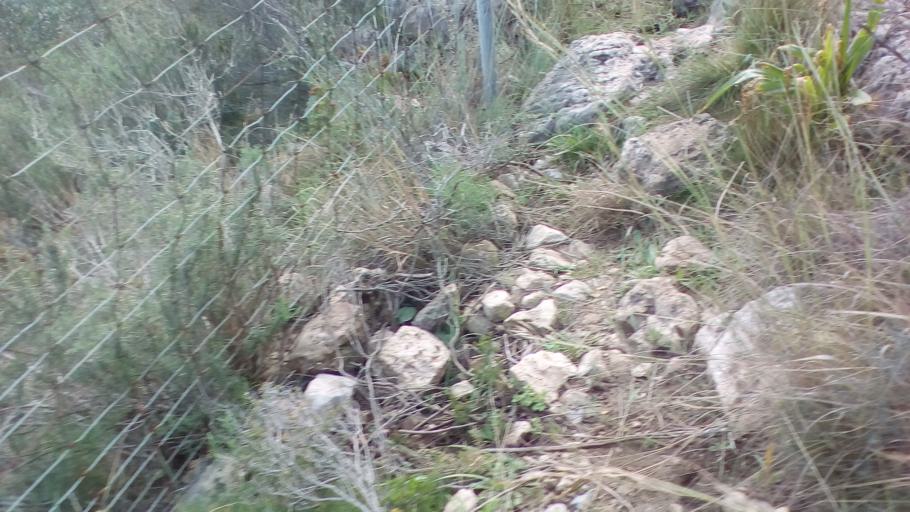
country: ES
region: Valencia
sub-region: Provincia de Valencia
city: Xeraco,Jaraco
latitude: 39.0519
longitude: -0.2301
